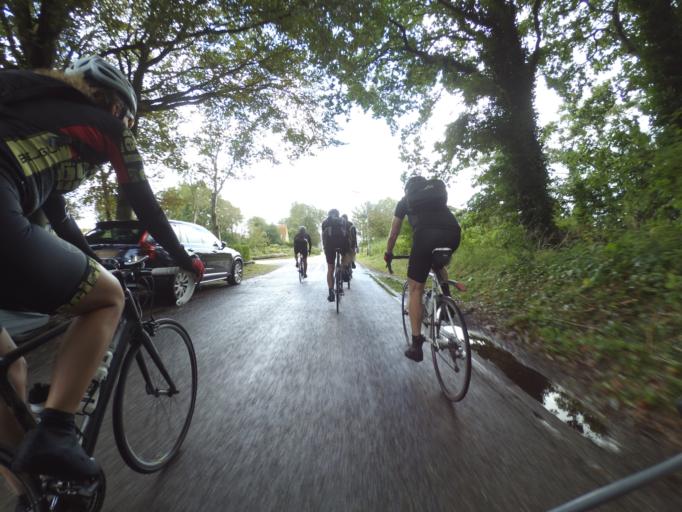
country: NL
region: North Holland
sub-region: Gemeente Heiloo
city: Heiloo
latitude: 52.6608
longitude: 4.6959
